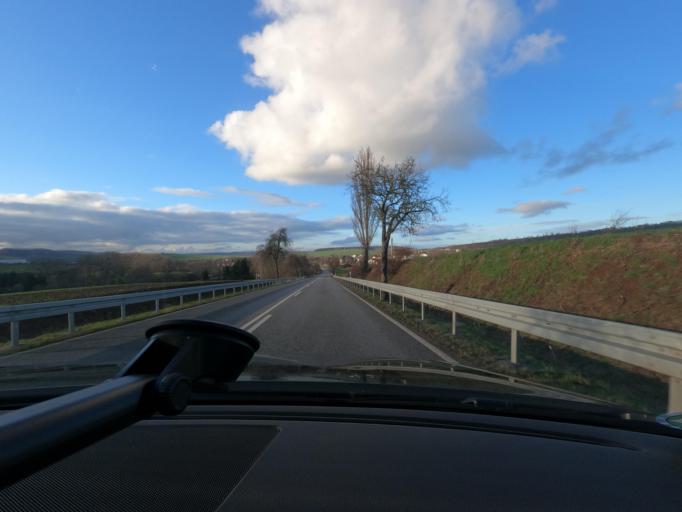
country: DE
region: Thuringia
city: Teistungen
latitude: 51.4651
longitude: 10.2815
